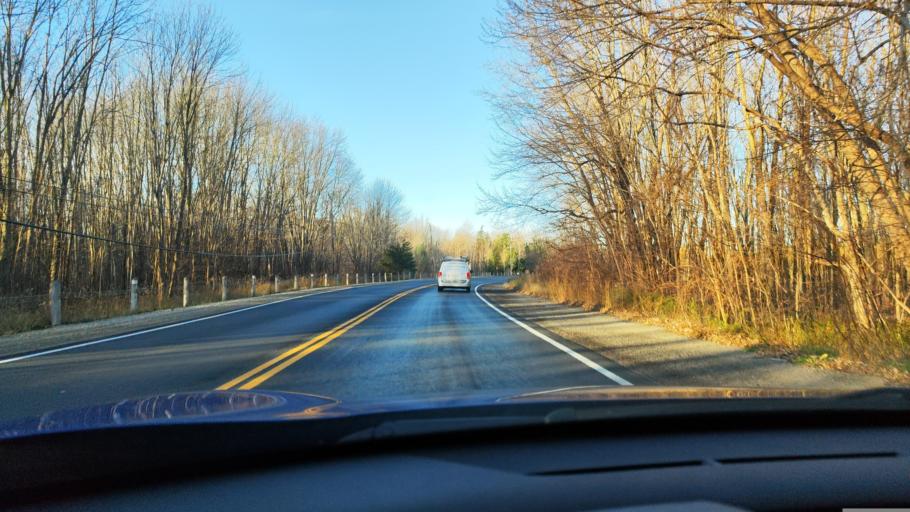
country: CA
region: Ontario
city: Angus
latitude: 44.3269
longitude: -79.9082
